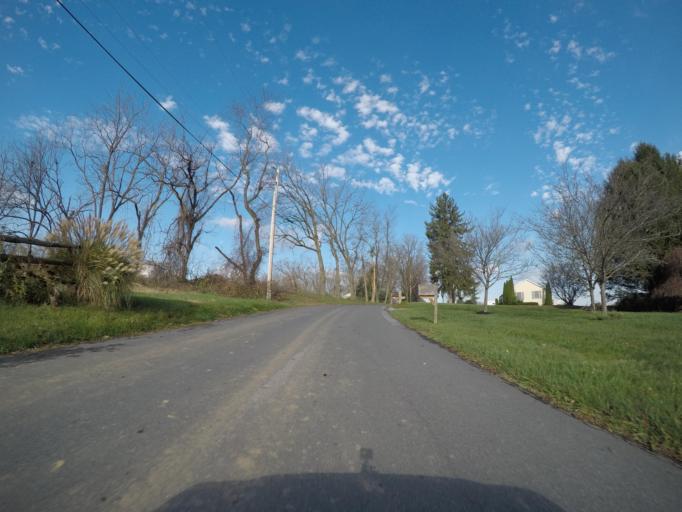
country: US
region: Maryland
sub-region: Carroll County
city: Hampstead
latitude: 39.5711
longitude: -76.8133
